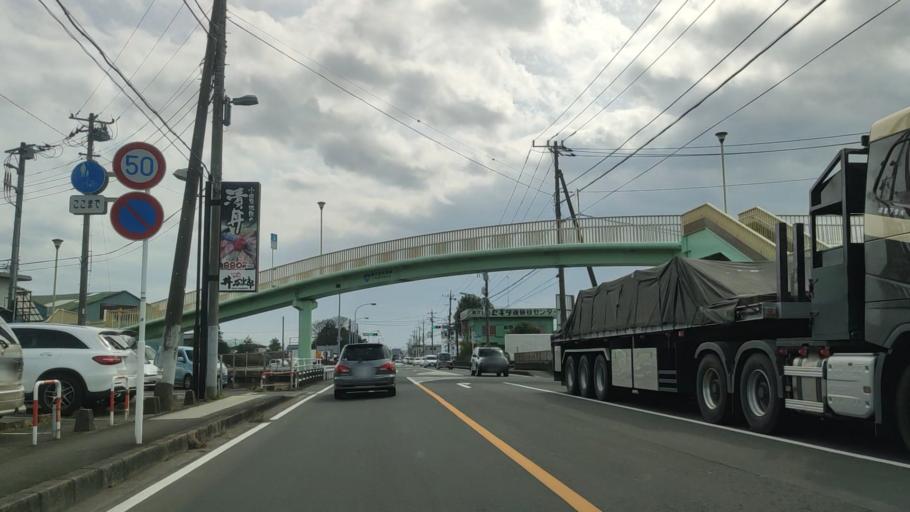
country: JP
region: Kanagawa
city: Odawara
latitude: 35.3097
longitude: 139.1638
